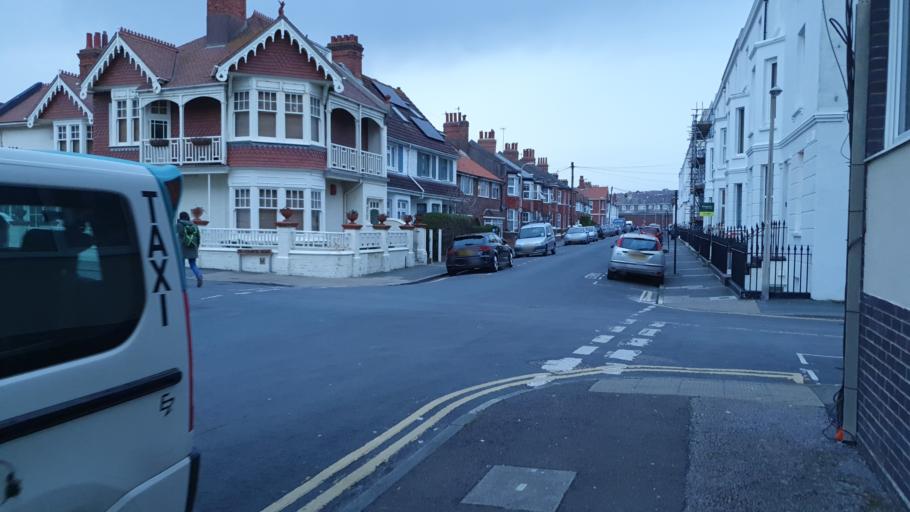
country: GB
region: England
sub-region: Brighton and Hove
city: Brighton
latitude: 50.8149
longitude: -0.1069
